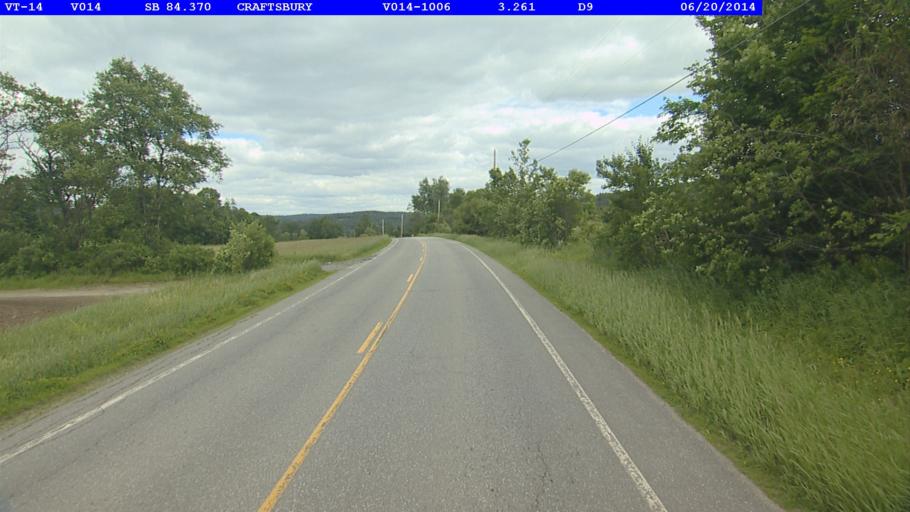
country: US
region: Vermont
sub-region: Caledonia County
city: Hardwick
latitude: 44.6385
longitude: -72.3994
